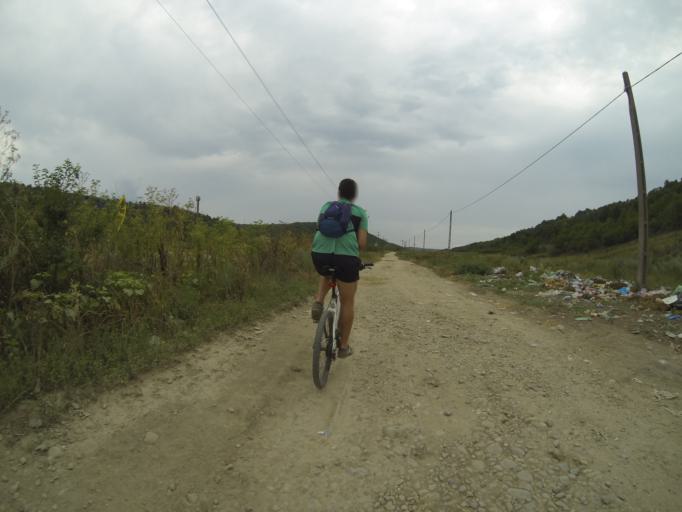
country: RO
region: Dolj
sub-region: Comuna Bradesti
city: Bradesti
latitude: 44.5020
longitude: 23.6461
